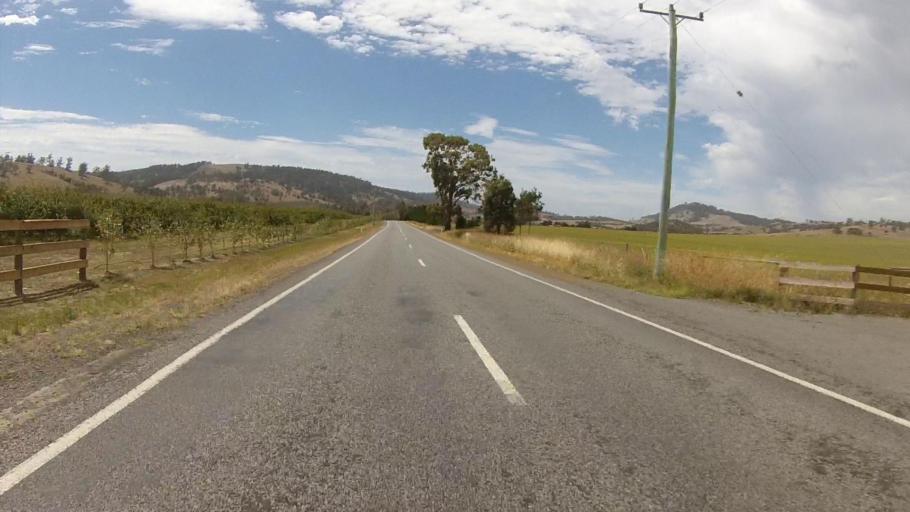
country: AU
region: Tasmania
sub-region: Sorell
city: Sorell
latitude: -42.6897
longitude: 147.4562
